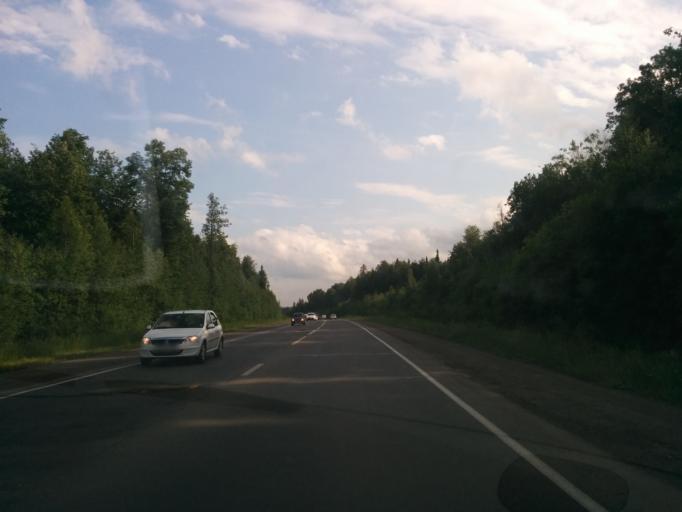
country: RU
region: Perm
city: Novyye Lyady
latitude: 58.1007
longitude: 56.4250
